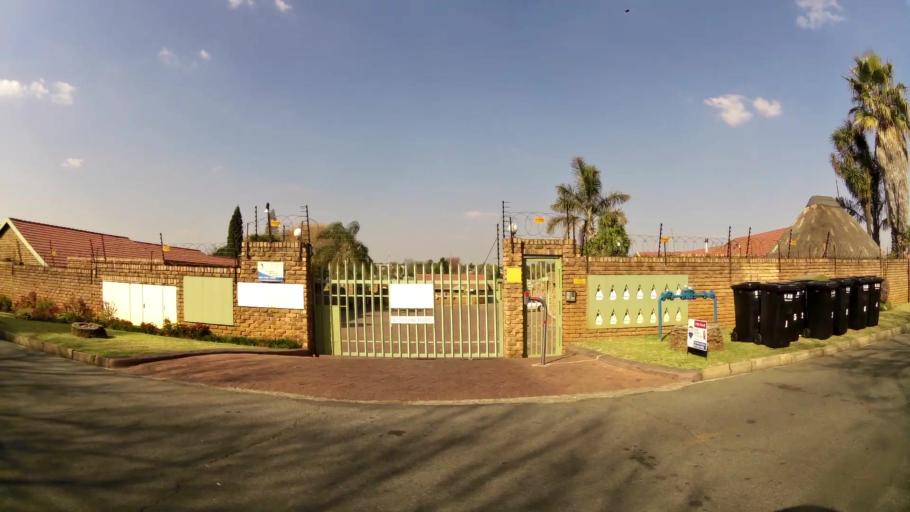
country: ZA
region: Gauteng
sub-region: City of Johannesburg Metropolitan Municipality
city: Modderfontein
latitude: -26.0906
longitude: 28.2172
